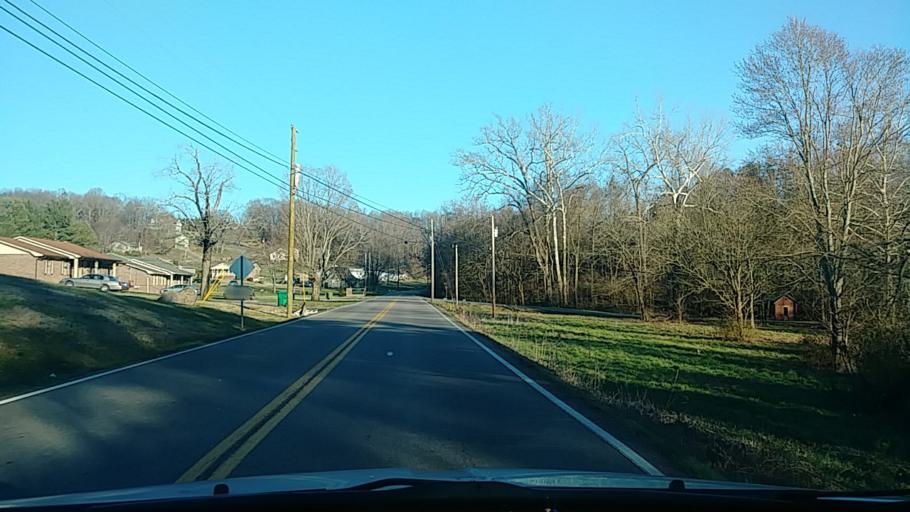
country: US
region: Tennessee
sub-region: Hamblen County
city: Morristown
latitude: 36.1880
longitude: -83.3825
